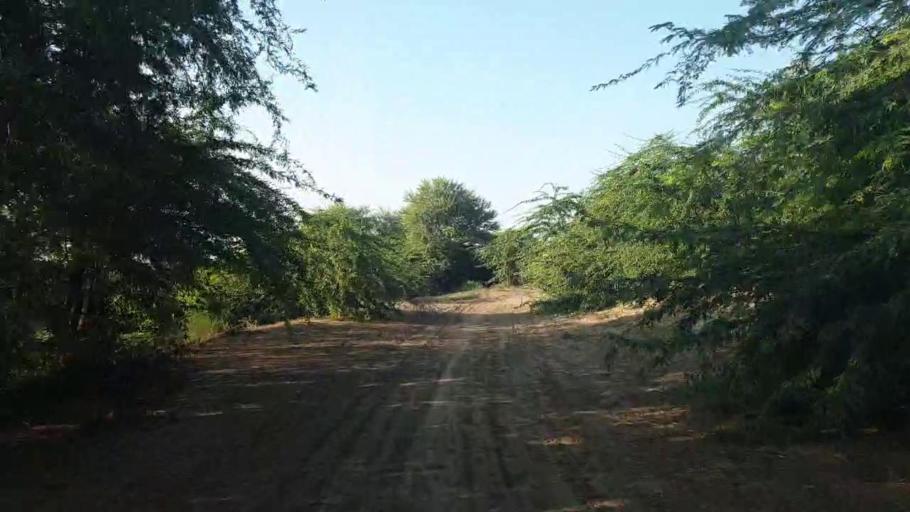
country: PK
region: Sindh
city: Badin
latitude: 24.6046
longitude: 68.7795
